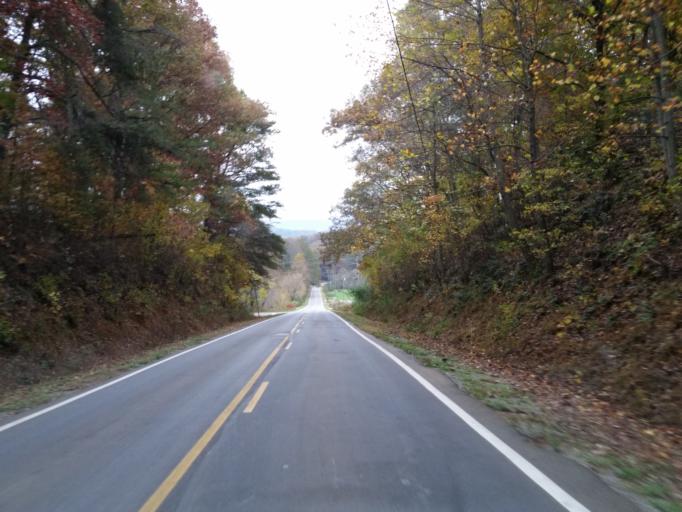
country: US
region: Georgia
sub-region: Gilmer County
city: Ellijay
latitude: 34.6451
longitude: -84.3412
